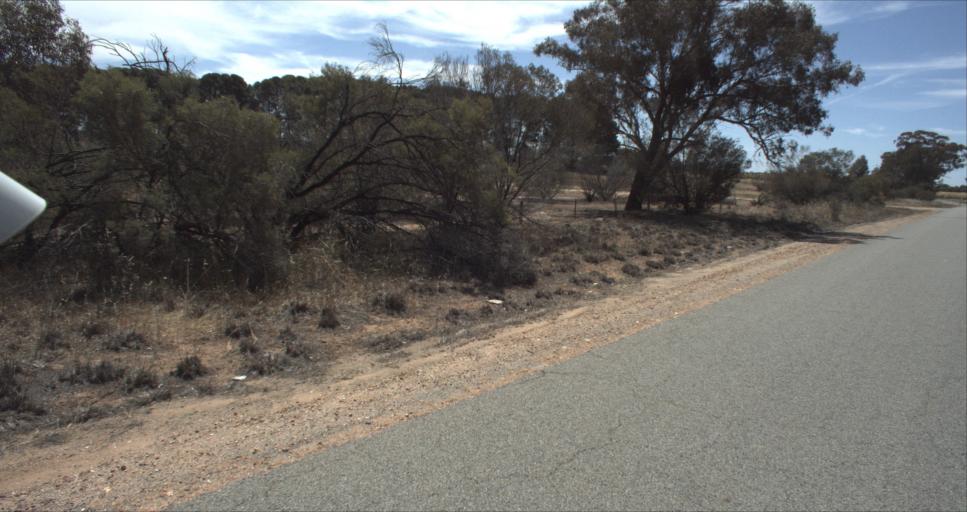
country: AU
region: New South Wales
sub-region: Leeton
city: Leeton
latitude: -34.6704
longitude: 146.4441
